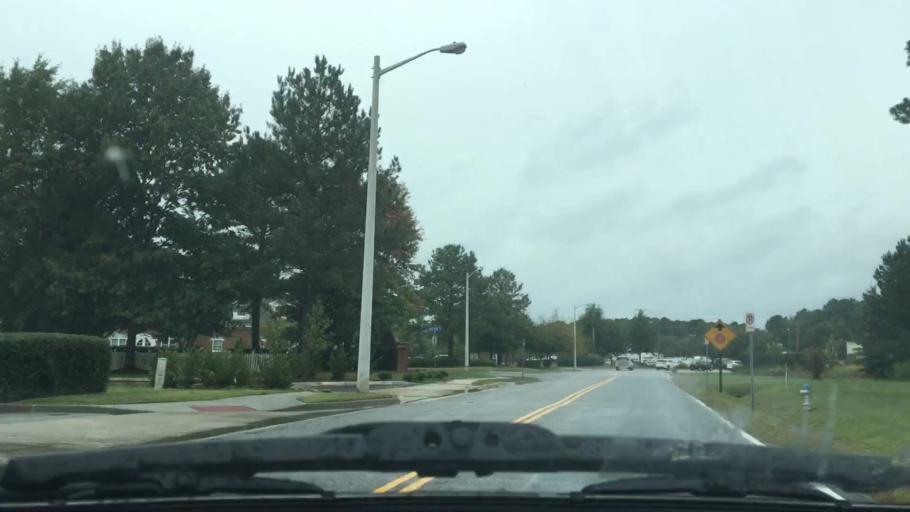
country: US
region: Virginia
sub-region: City of Chesapeake
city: Chesapeake
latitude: 36.6849
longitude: -76.2304
